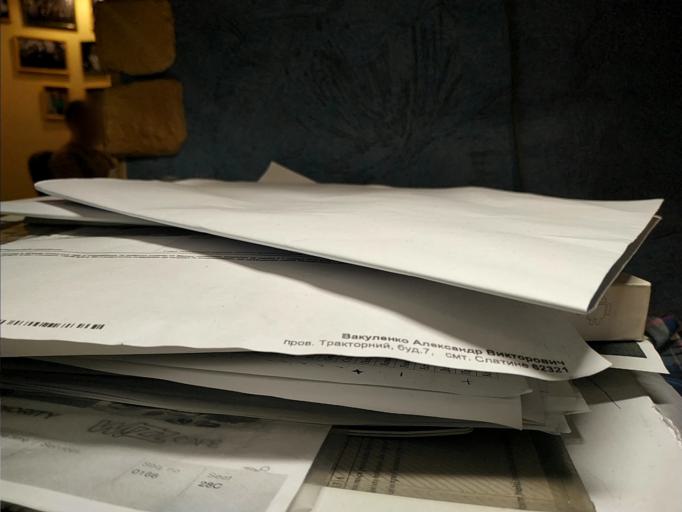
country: RU
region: Tverskaya
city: Zubtsov
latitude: 56.1268
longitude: 34.5357
